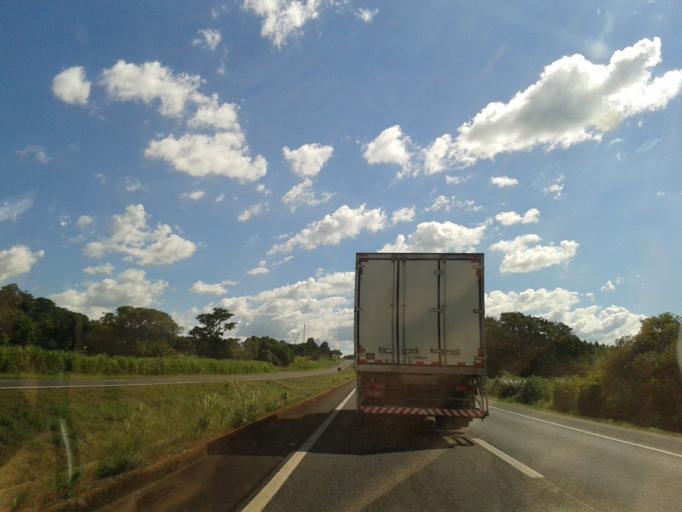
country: BR
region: Goias
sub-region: Morrinhos
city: Morrinhos
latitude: -17.7911
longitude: -49.1992
